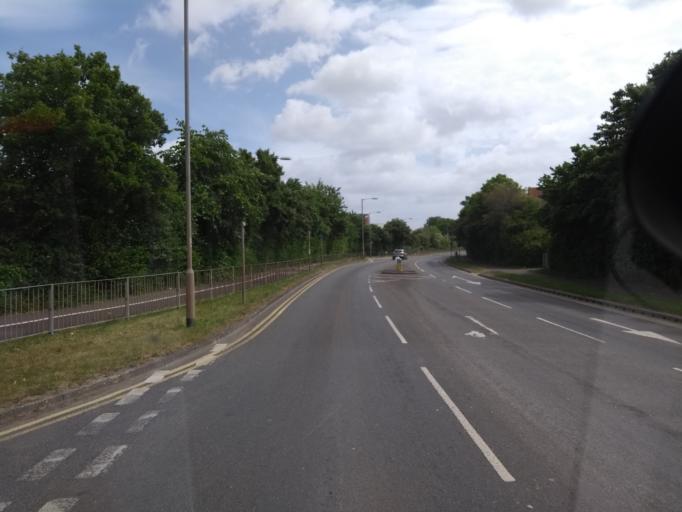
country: GB
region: England
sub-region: Somerset
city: Bridgwater
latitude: 51.1387
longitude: -3.0112
